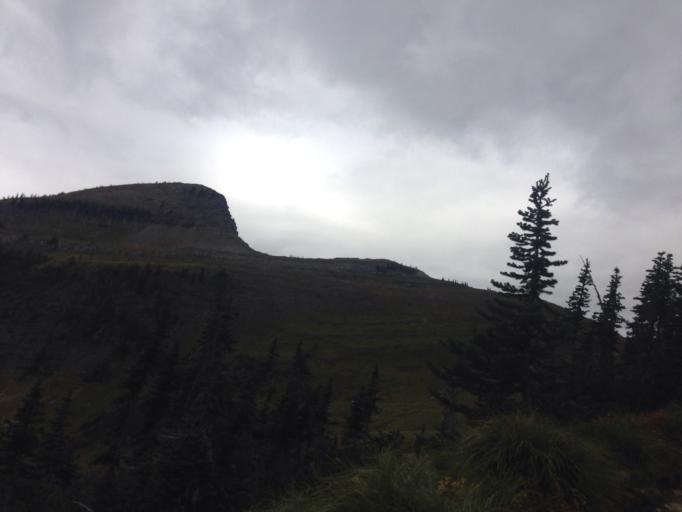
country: US
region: Montana
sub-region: Flathead County
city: Columbia Falls
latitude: 48.7317
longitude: -113.7204
